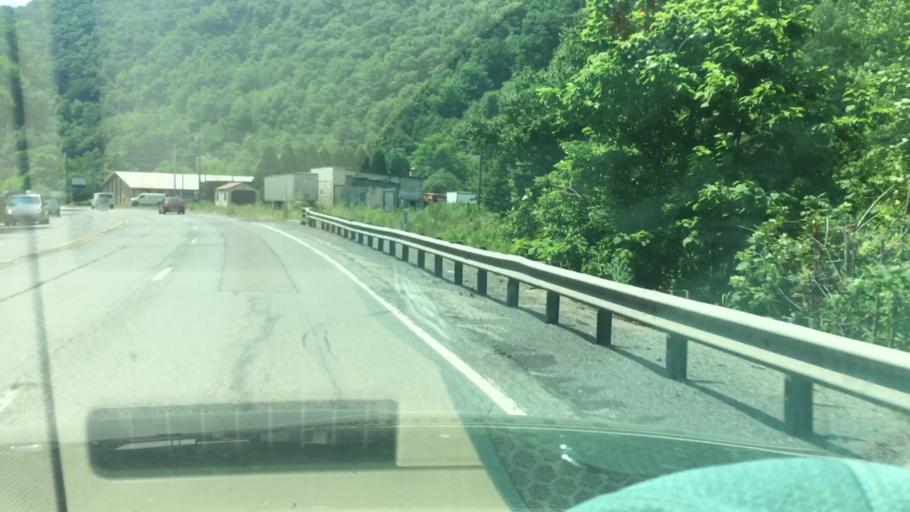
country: US
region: Pennsylvania
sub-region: Schuylkill County
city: Tamaqua
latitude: 40.7792
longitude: -75.9610
